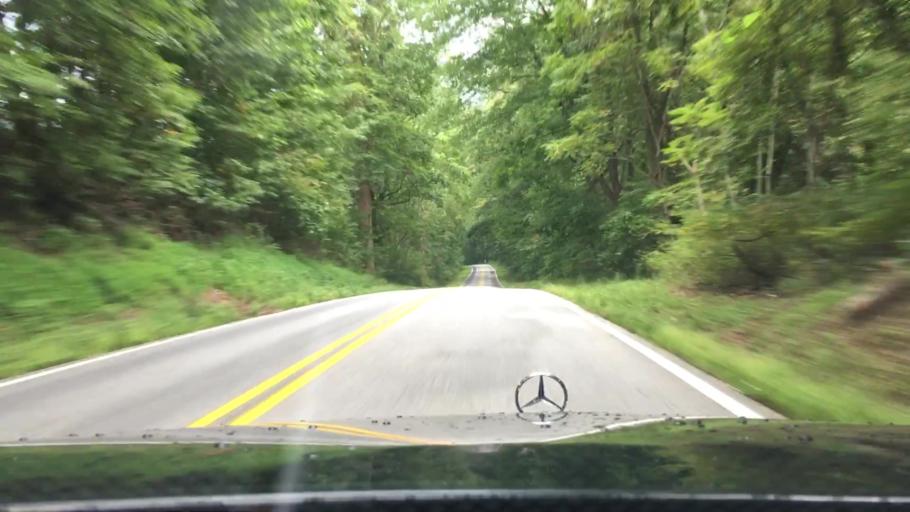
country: US
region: Virginia
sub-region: Nelson County
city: Nellysford
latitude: 37.8431
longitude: -78.9275
